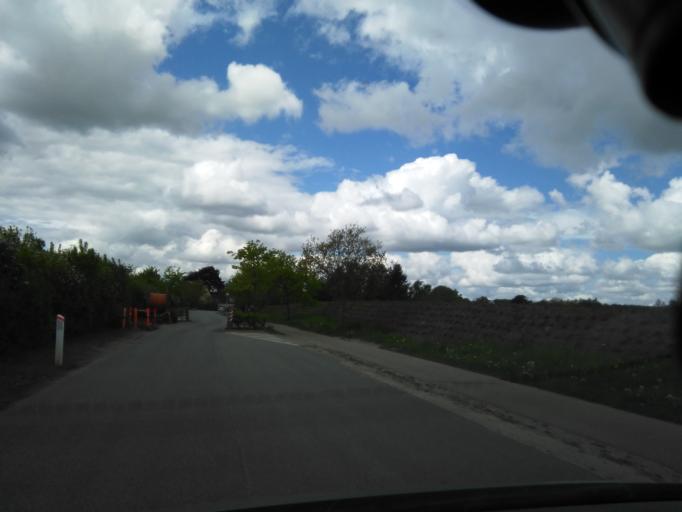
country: DK
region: Central Jutland
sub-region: Skanderborg Kommune
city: Horning
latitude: 56.0792
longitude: 10.0479
